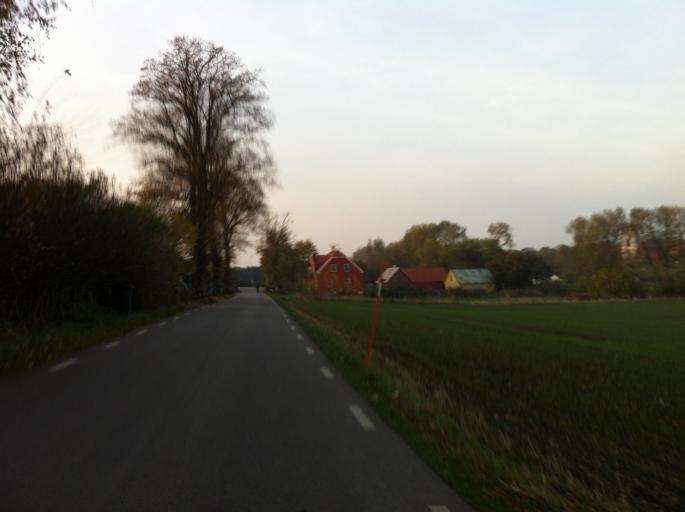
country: SE
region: Skane
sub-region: Landskrona
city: Asmundtorp
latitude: 55.8765
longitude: 13.0036
